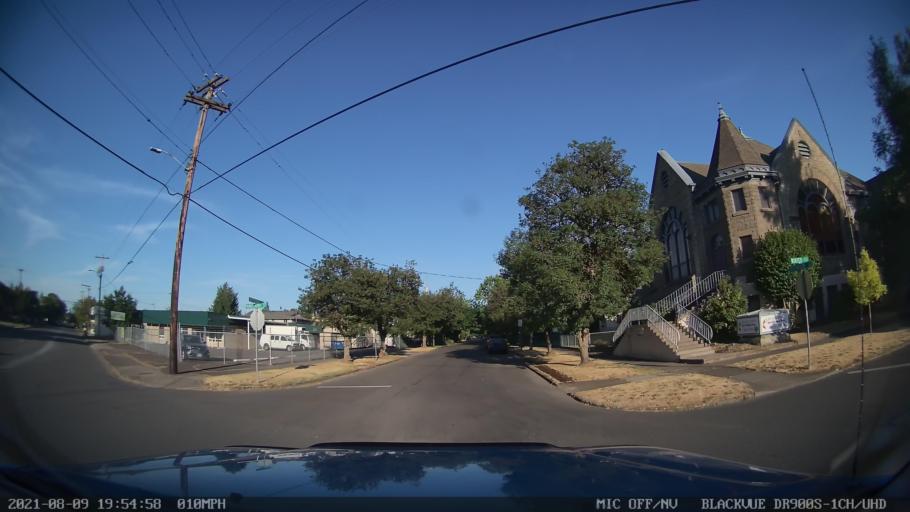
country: US
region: Oregon
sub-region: Marion County
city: Salem
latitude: 44.9541
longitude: -123.0245
